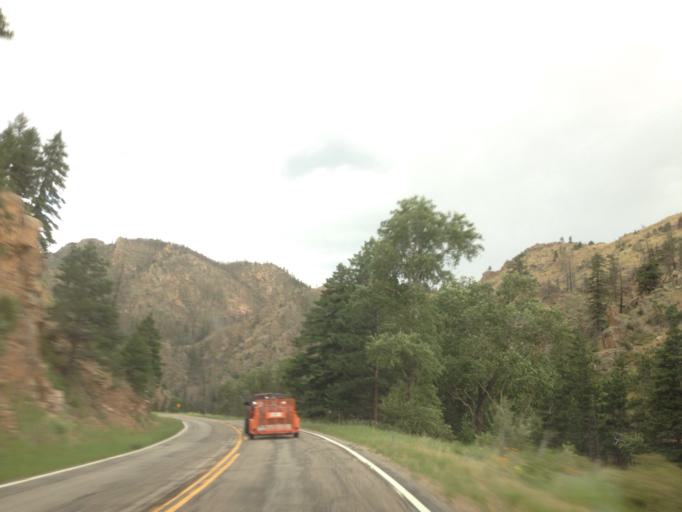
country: US
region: Colorado
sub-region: Larimer County
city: Laporte
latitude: 40.6861
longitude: -105.4334
